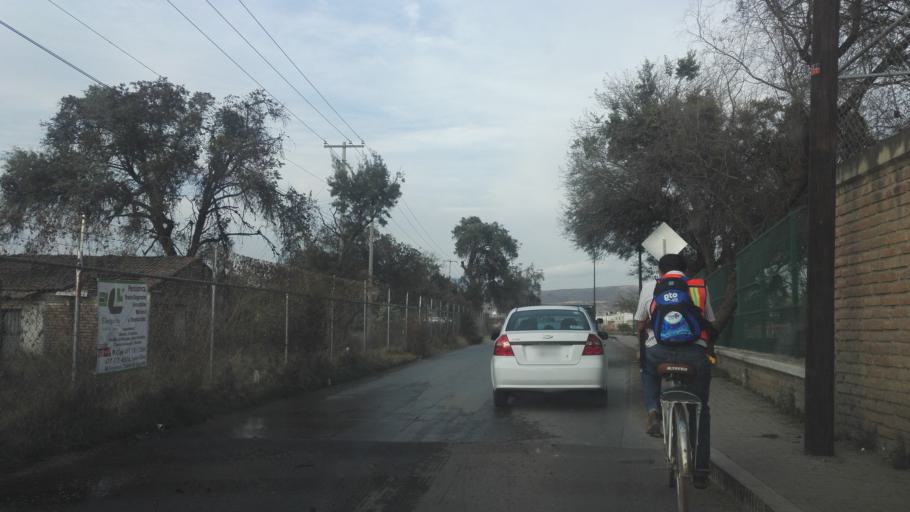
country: MX
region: Guanajuato
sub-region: Leon
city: Fraccionamiento Paraiso Real
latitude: 21.0796
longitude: -101.6023
